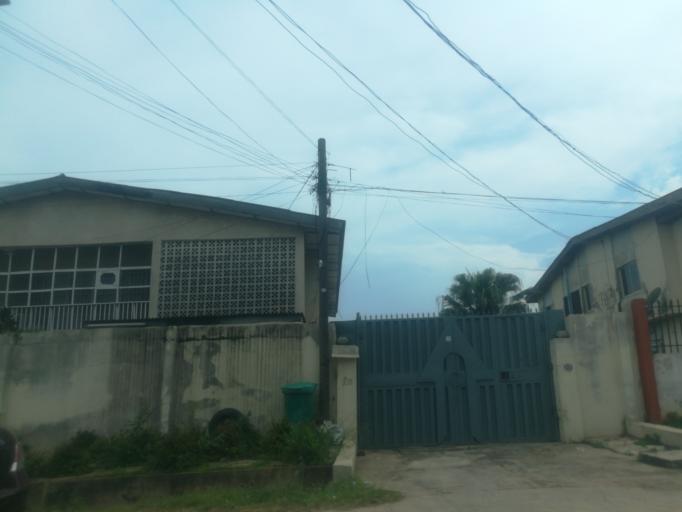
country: NG
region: Oyo
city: Ibadan
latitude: 7.4232
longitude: 3.9131
